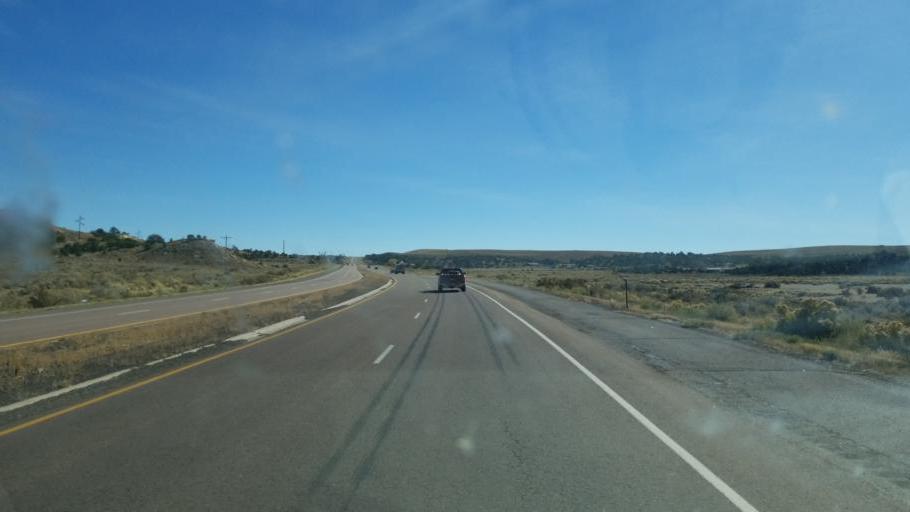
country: US
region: Arizona
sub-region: Apache County
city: Window Rock
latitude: 35.6397
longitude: -109.0153
